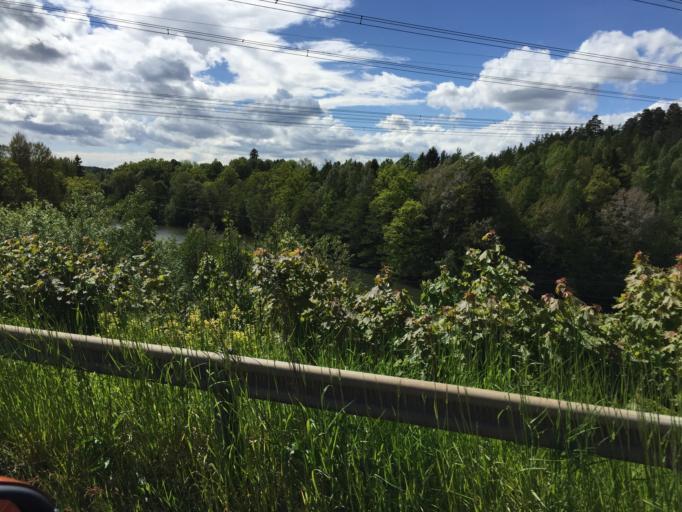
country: SE
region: OEstergoetland
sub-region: Norrkopings Kommun
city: Kimstad
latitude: 58.5309
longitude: 15.9699
